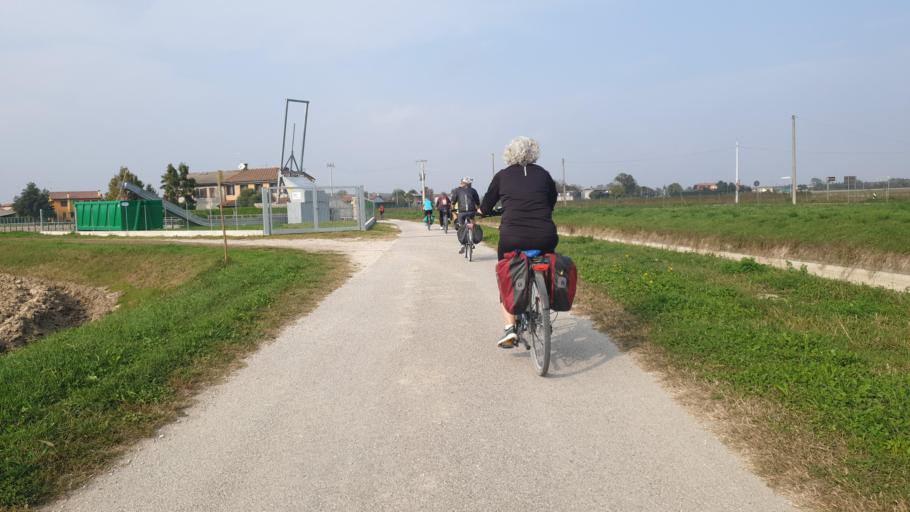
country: IT
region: Veneto
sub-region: Provincia di Padova
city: Corte
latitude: 45.2944
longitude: 12.0837
